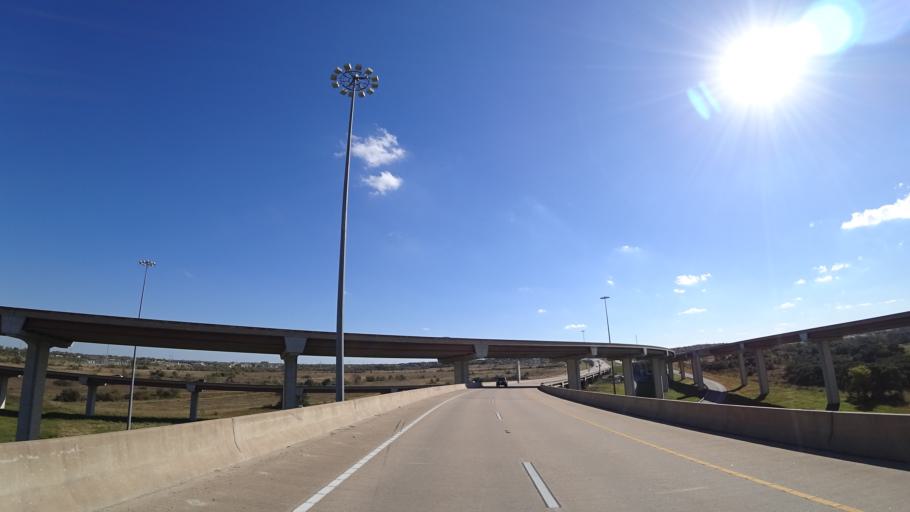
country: US
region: Texas
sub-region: Travis County
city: Wells Branch
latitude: 30.4756
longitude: -97.7027
